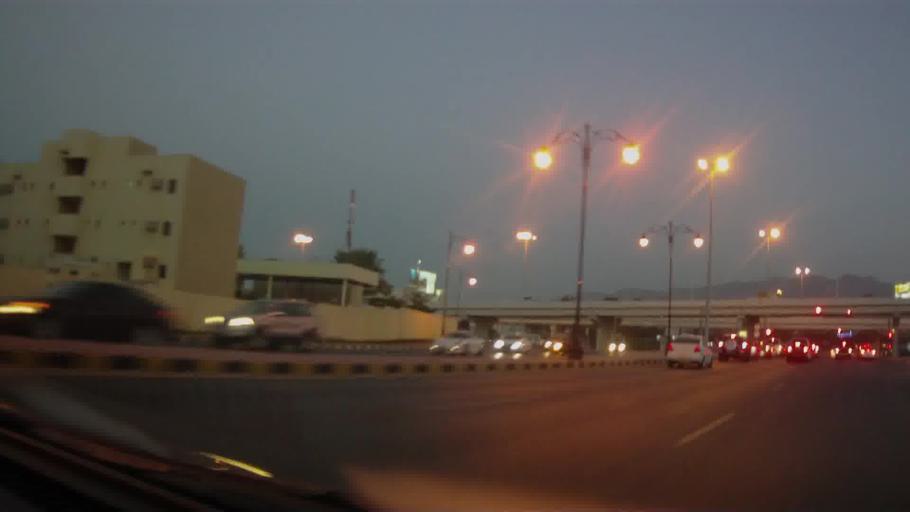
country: OM
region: Muhafazat Masqat
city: Bawshar
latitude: 23.5991
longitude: 58.4423
